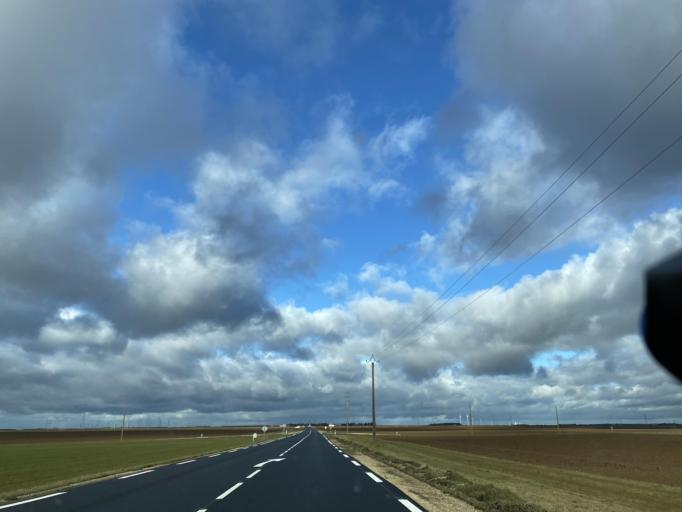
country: FR
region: Centre
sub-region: Departement d'Eure-et-Loir
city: Baigneaux
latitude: 48.1806
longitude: 1.8333
